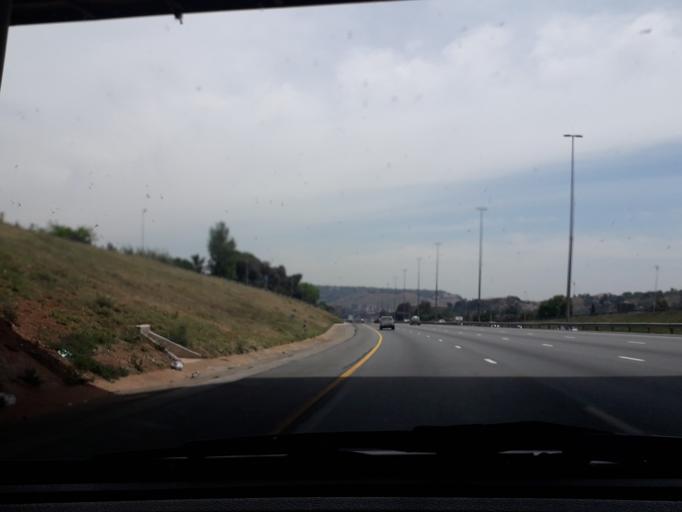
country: ZA
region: Gauteng
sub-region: City of Johannesburg Metropolitan Municipality
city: Roodepoort
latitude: -26.1663
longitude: 27.9401
